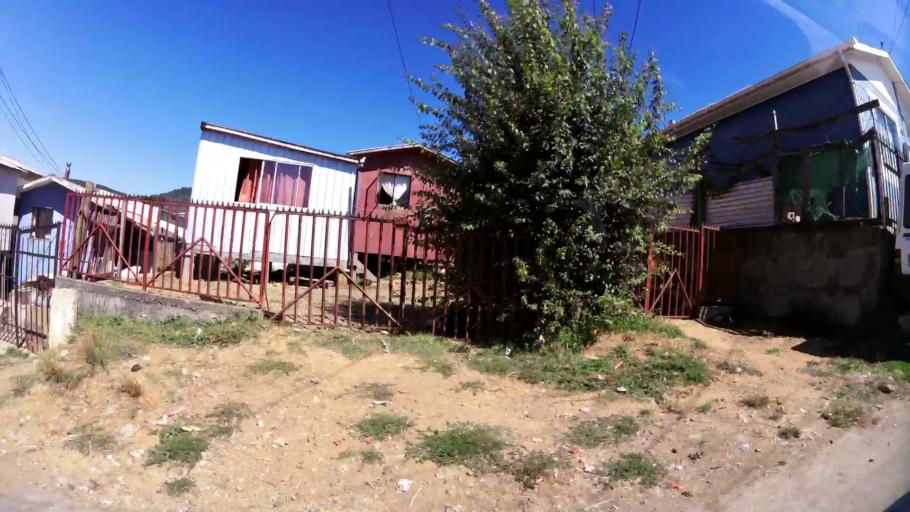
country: CL
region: Biobio
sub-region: Provincia de Concepcion
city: Penco
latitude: -36.7284
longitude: -72.9838
